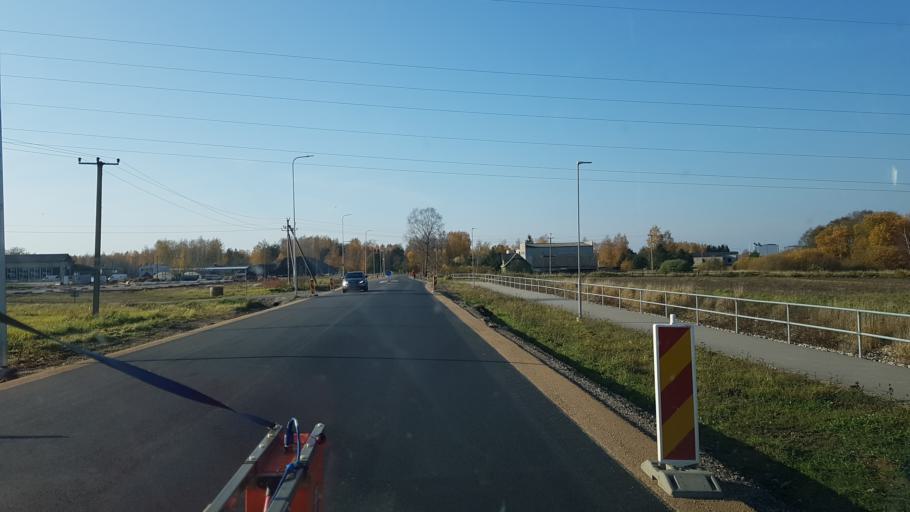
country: EE
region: Vorumaa
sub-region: Antsla vald
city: Vana-Antsla
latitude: 57.8394
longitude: 26.4869
